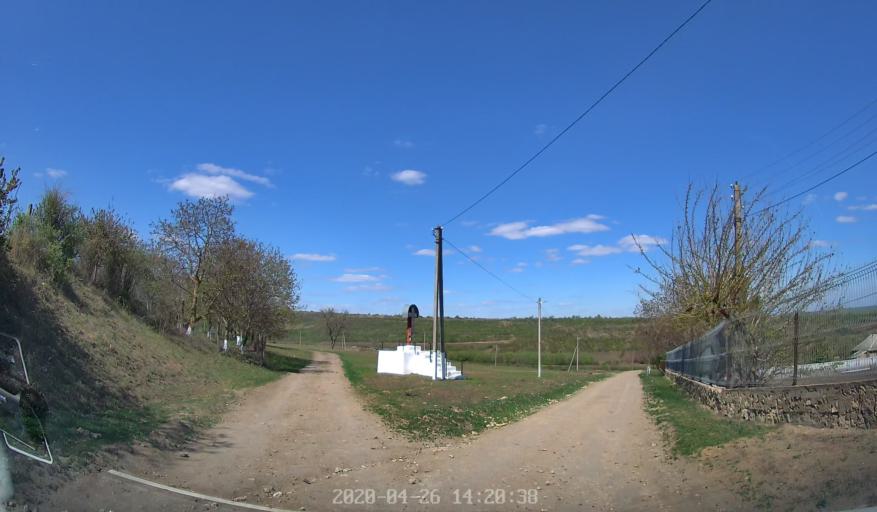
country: MD
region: Telenesti
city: Cocieri
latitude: 47.3580
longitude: 29.0581
